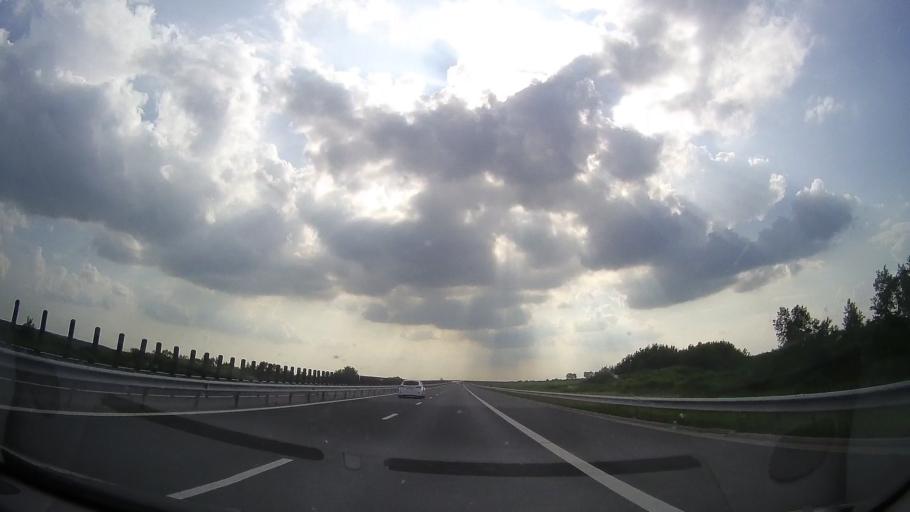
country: RO
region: Timis
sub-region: Comuna Bethausen
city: Bethausen
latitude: 45.8074
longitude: 21.9205
